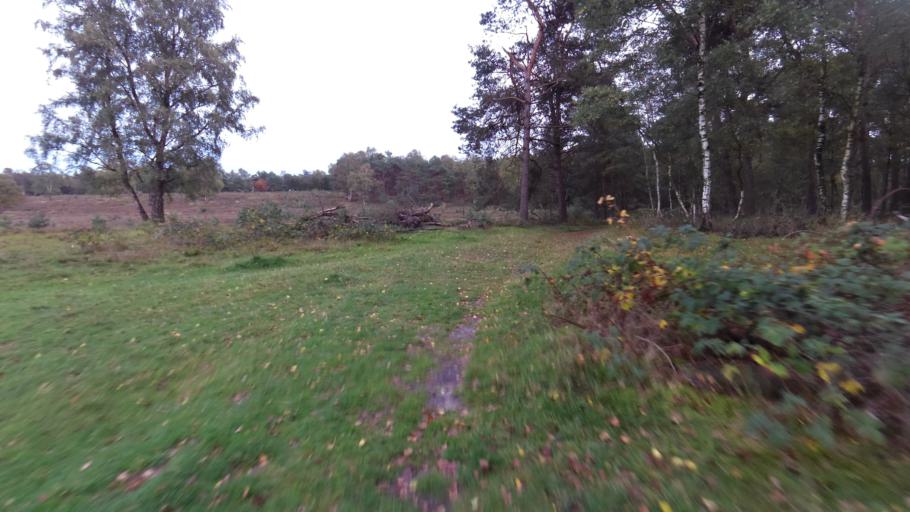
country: NL
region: Gelderland
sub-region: Gemeente Renkum
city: Wolfheze
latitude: 52.0085
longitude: 5.8054
